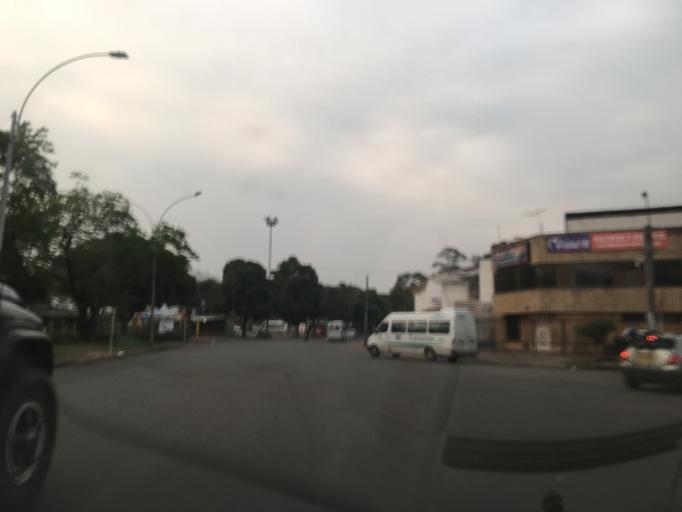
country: CO
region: Valle del Cauca
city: Cali
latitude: 3.4648
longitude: -76.5231
